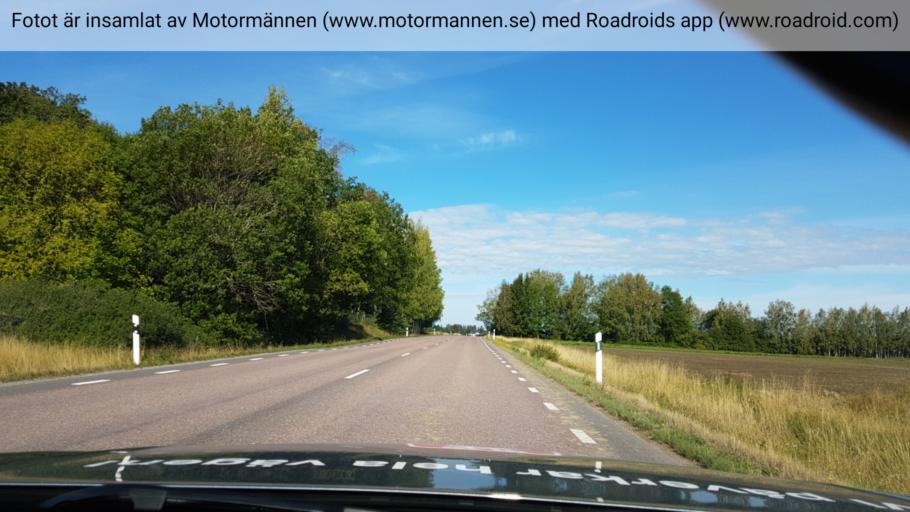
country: SE
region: Uppsala
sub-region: Uppsala Kommun
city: Gamla Uppsala
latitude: 59.8860
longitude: 17.5635
